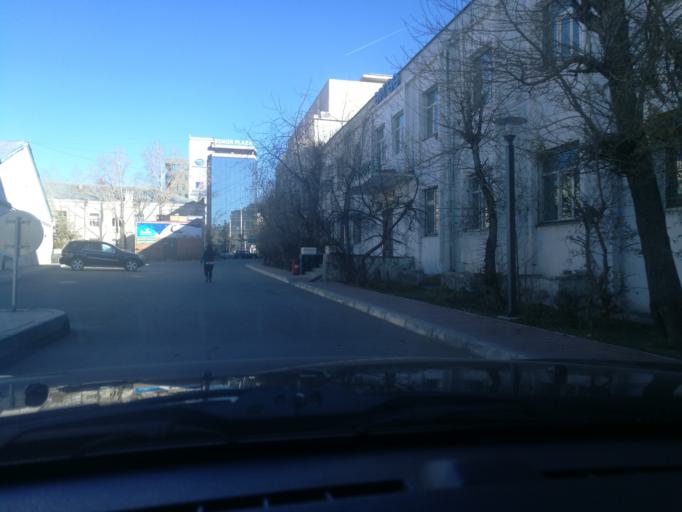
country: MN
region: Ulaanbaatar
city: Ulaanbaatar
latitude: 47.9170
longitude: 106.9272
